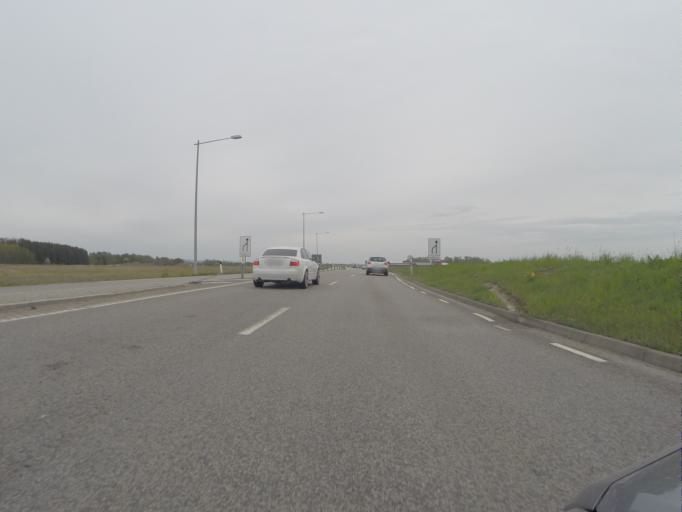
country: SE
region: Skane
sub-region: Helsingborg
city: Hyllinge
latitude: 56.0959
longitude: 12.8589
